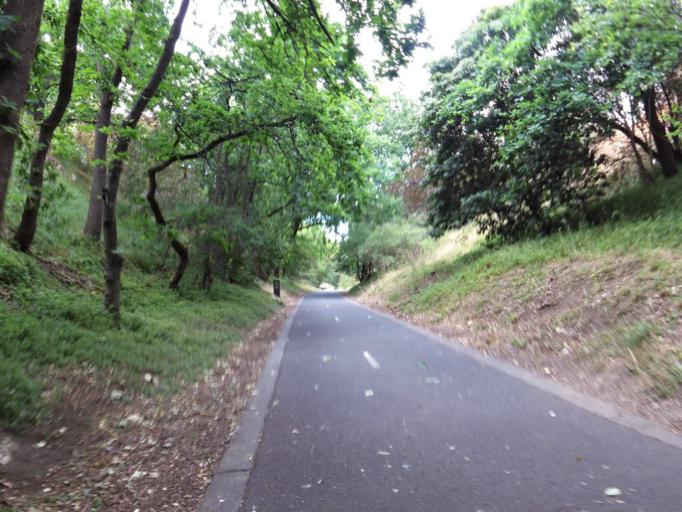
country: AU
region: Victoria
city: Balwyn
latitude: -37.8169
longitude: 145.0656
